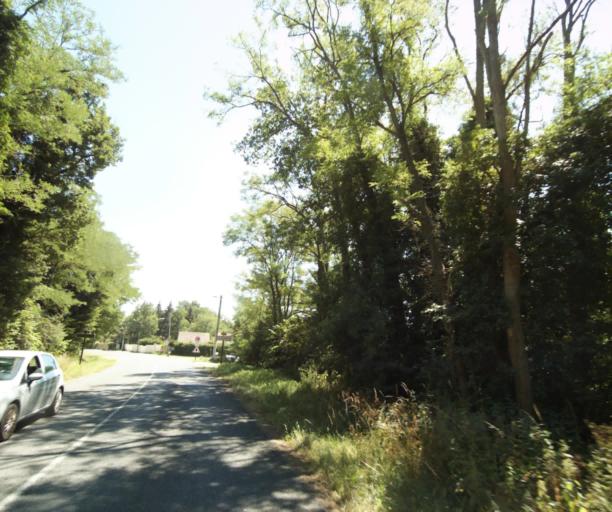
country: FR
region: Ile-de-France
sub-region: Departement de Seine-et-Marne
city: Noisy-sur-Ecole
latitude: 48.3651
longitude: 2.5173
